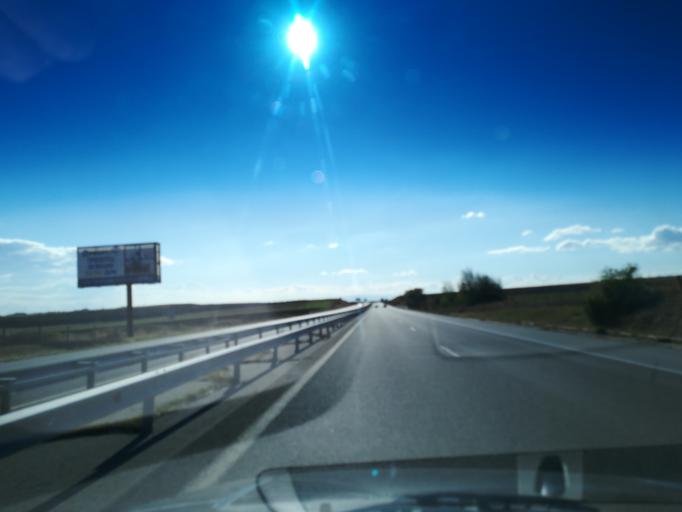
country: BG
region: Stara Zagora
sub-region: Obshtina Nikolaevo
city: Elkhovo
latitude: 42.2660
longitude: 25.4384
